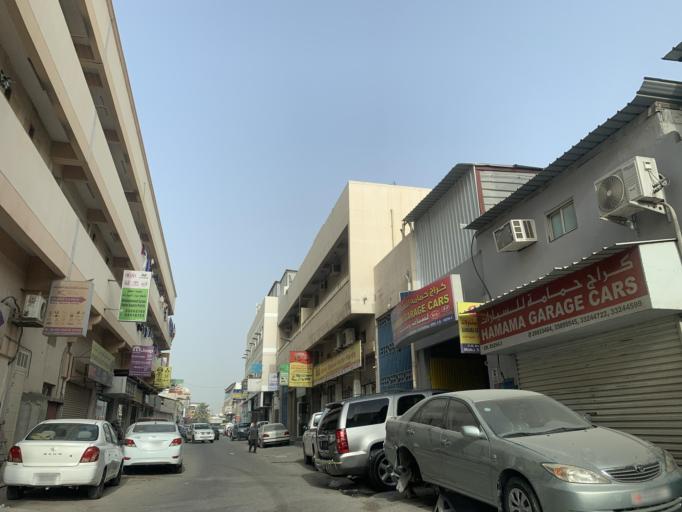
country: BH
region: Northern
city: Madinat `Isa
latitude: 26.1850
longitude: 50.5314
